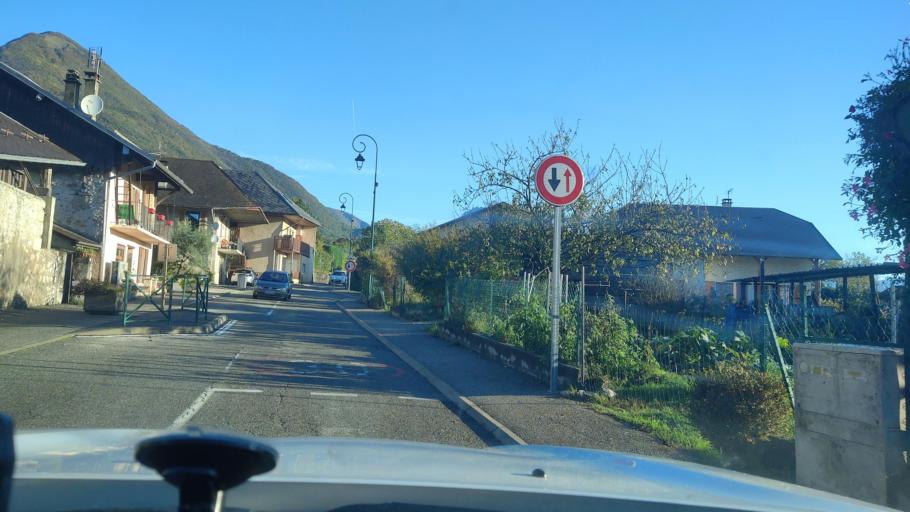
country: FR
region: Rhone-Alpes
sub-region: Departement de la Savoie
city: Cruet
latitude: 45.5231
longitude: 6.0912
